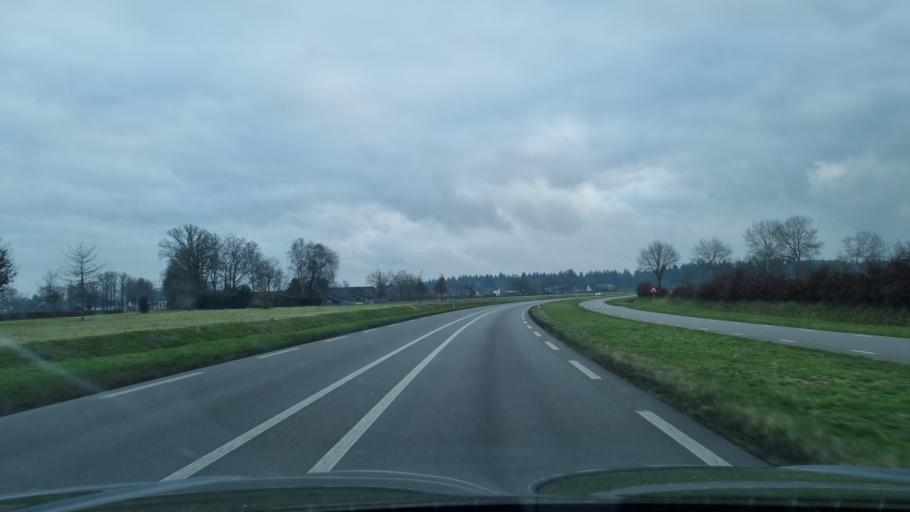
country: NL
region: Gelderland
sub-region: Gemeente Bronckhorst
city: Baak
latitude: 52.0100
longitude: 6.2296
